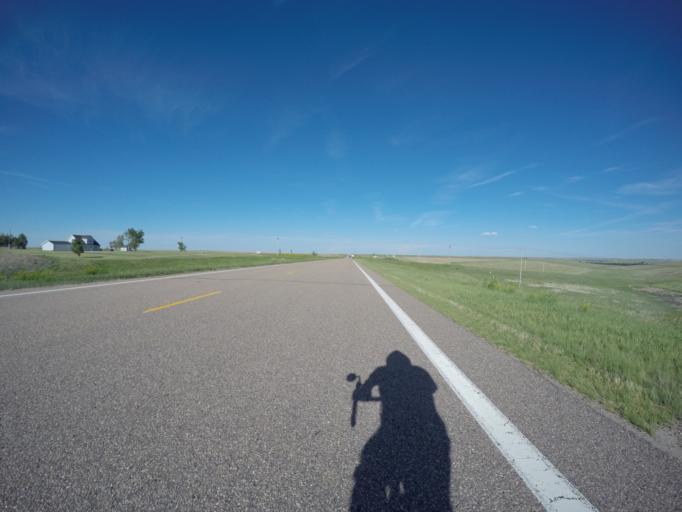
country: US
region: Kansas
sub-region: Cheyenne County
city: Saint Francis
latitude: 39.7570
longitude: -101.9014
